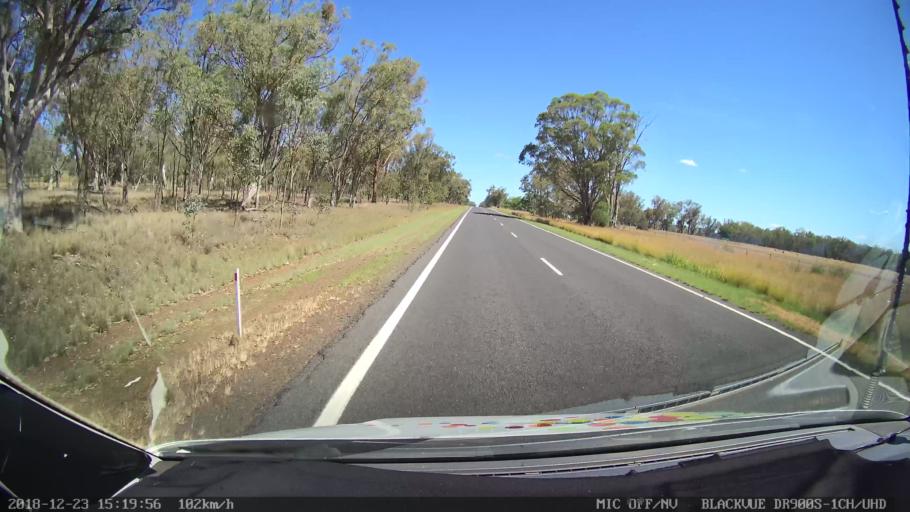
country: AU
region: New South Wales
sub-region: Tamworth Municipality
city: Manilla
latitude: -30.8357
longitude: 150.7862
